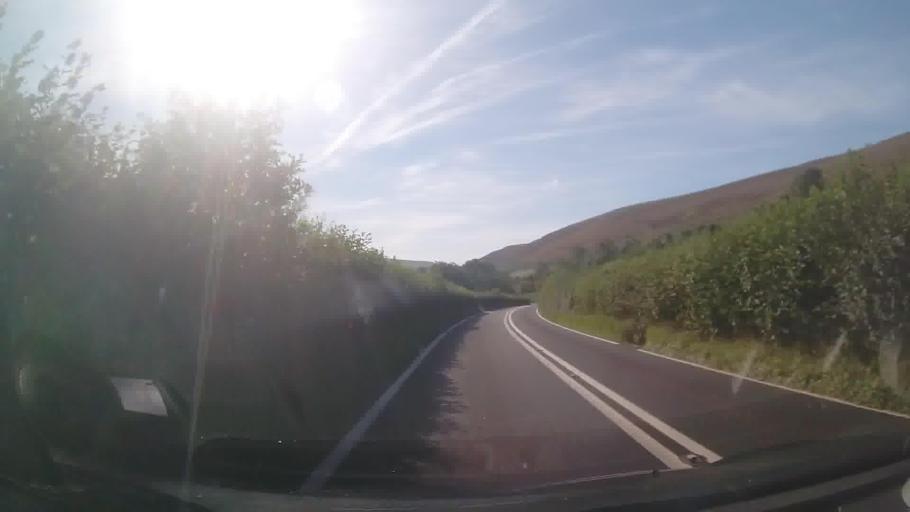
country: GB
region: Wales
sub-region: Sir Powys
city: Hay
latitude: 51.9622
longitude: -3.2052
